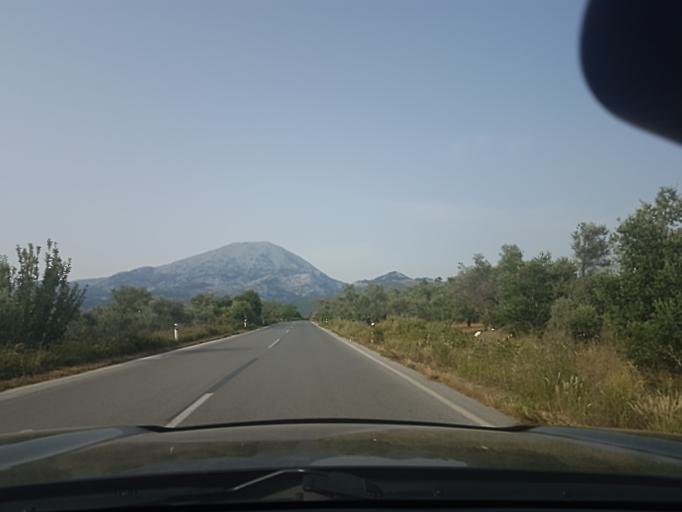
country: GR
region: Central Greece
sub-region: Nomos Evvoias
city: Afration
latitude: 38.5693
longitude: 23.7918
